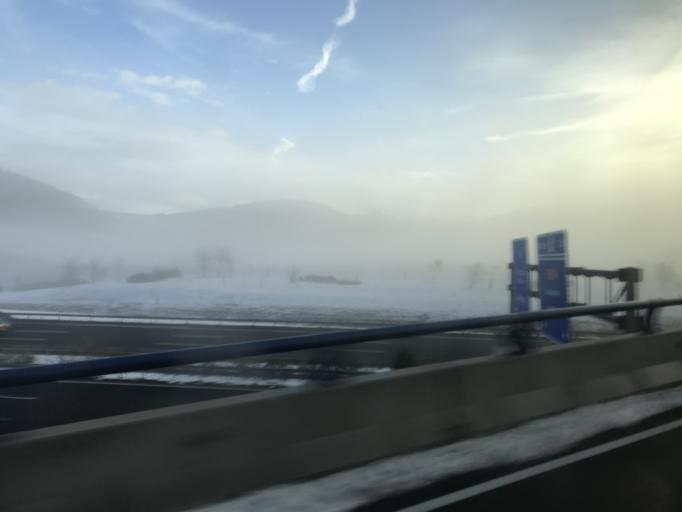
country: ES
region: Basque Country
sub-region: Provincia de Alava
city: Arminon
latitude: 42.7256
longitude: -2.8701
